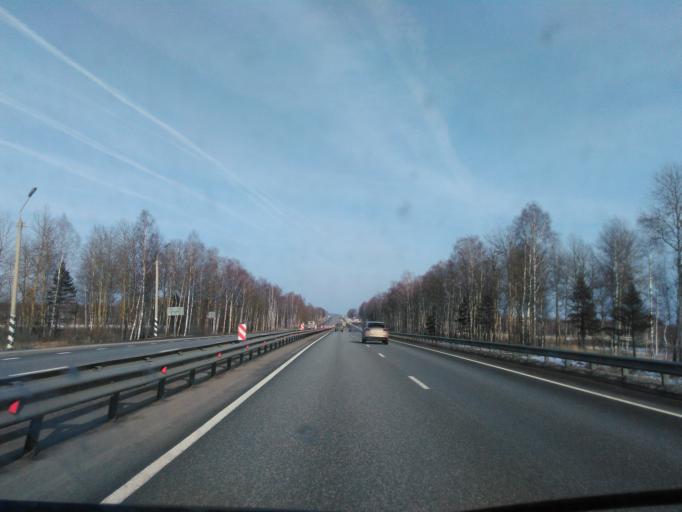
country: RU
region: Smolensk
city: Verkhnedneprovskiy
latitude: 55.1745
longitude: 33.4399
